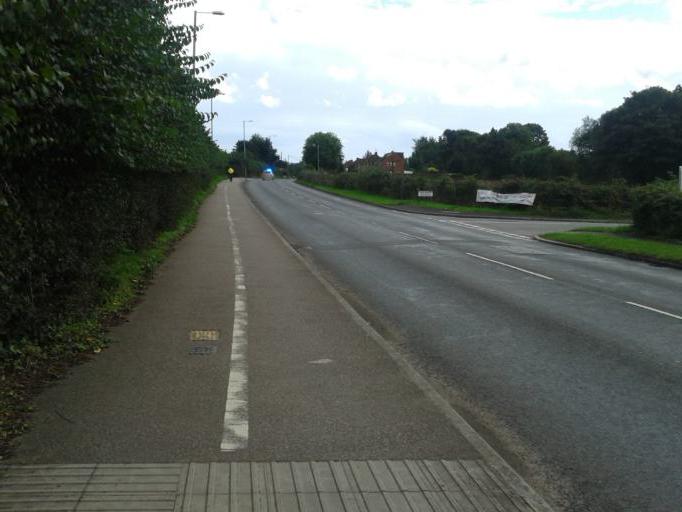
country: GB
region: England
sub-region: Devon
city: Topsham
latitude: 50.6916
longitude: -3.4769
